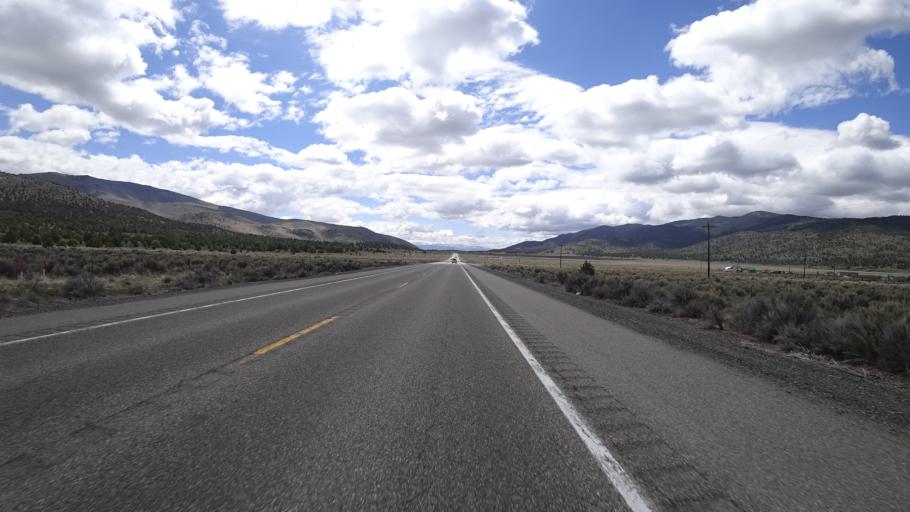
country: US
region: Nevada
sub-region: Douglas County
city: Gardnerville Ranchos
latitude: 38.8000
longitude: -119.6042
